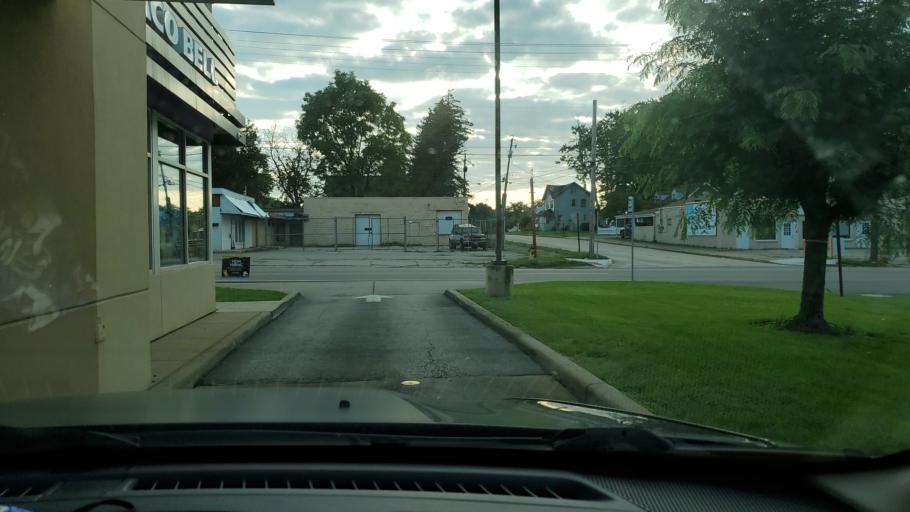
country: US
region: Ohio
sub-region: Mahoning County
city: Struthers
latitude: 41.0560
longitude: -80.6162
